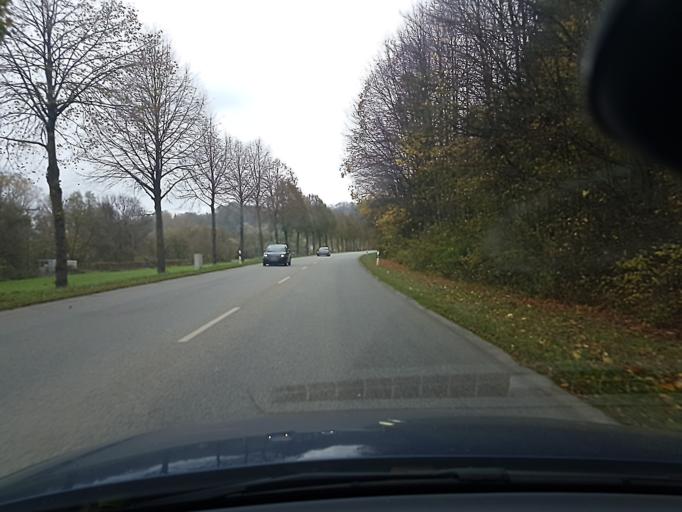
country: DE
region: Bavaria
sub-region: Lower Bavaria
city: Stallwang
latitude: 48.5684
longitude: 12.2234
